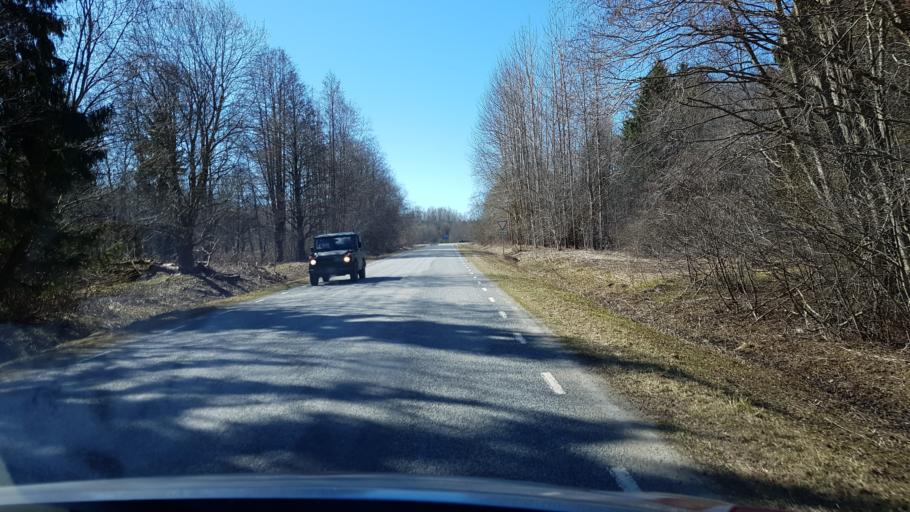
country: EE
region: Laeaene-Virumaa
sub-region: Haljala vald
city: Haljala
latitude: 59.4586
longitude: 26.2320
